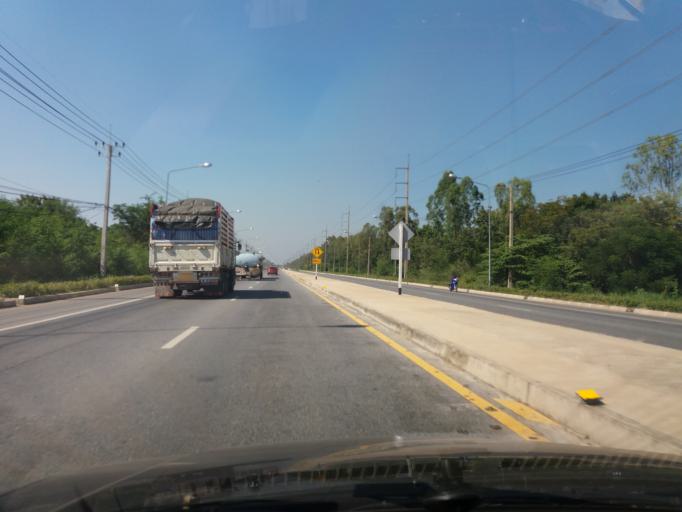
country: TH
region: Chai Nat
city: Chai Nat
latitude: 15.2408
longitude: 100.1031
